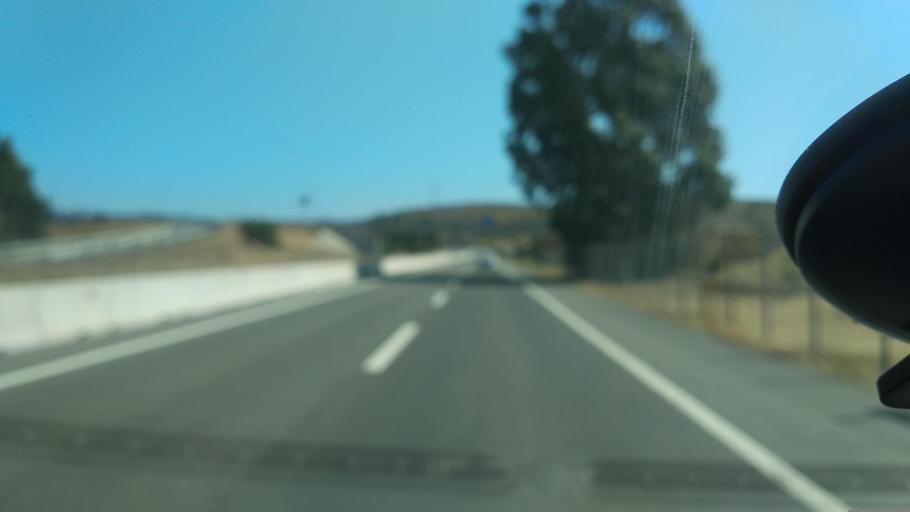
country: CL
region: Valparaiso
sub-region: Provincia de Marga Marga
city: Limache
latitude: -32.9904
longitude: -71.3277
